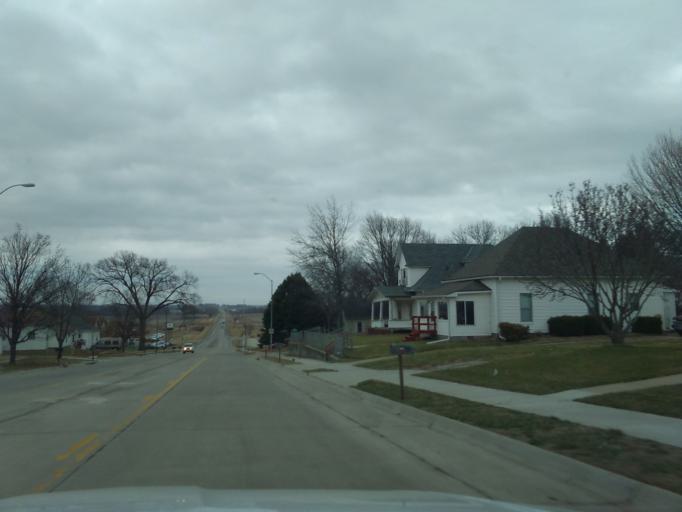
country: US
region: Nebraska
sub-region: Nemaha County
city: Auburn
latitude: 40.3928
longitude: -95.8357
